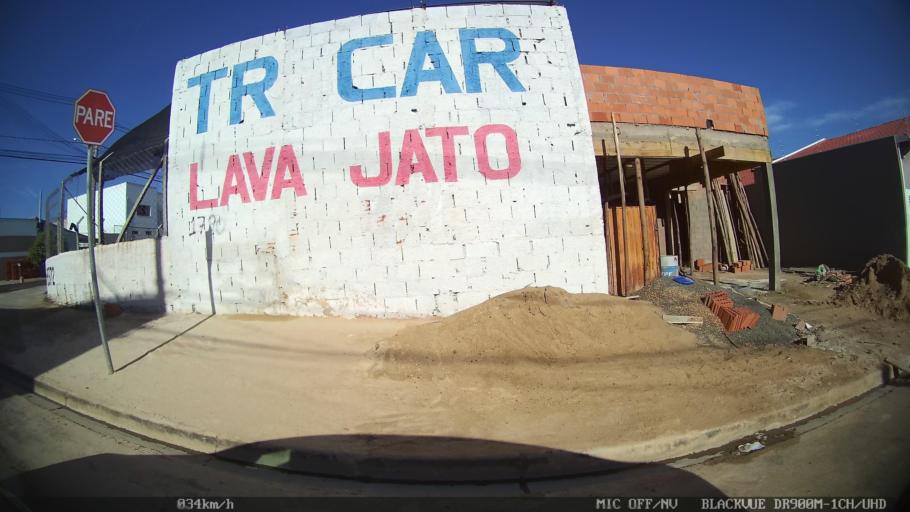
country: BR
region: Sao Paulo
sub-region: Franca
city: Franca
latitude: -20.5116
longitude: -47.4269
